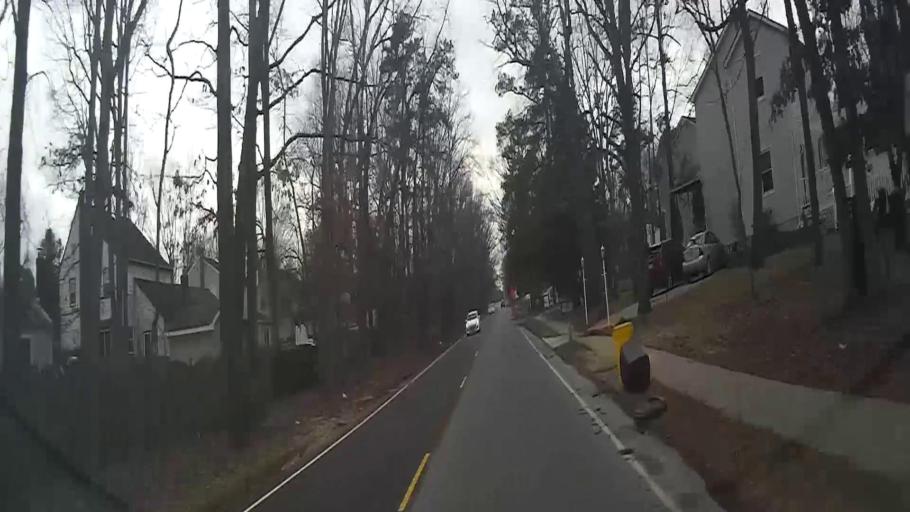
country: US
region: New Jersey
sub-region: Camden County
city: Pine Hill
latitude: 39.7787
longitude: -74.9893
